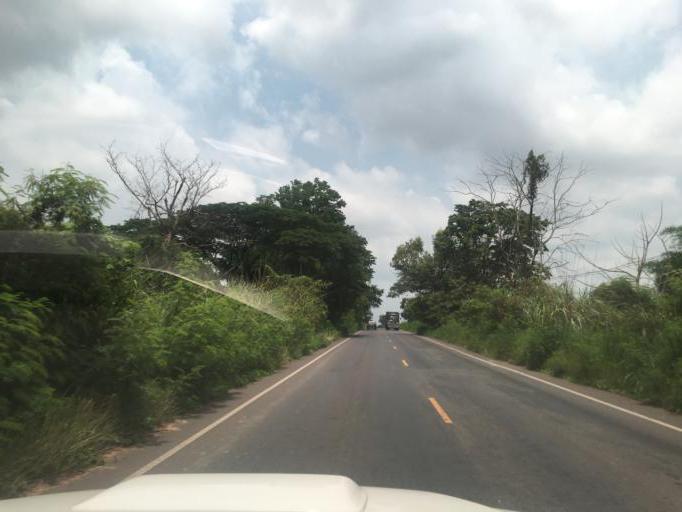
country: TH
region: Changwat Udon Thani
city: Udon Thani
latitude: 17.3104
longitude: 102.7091
